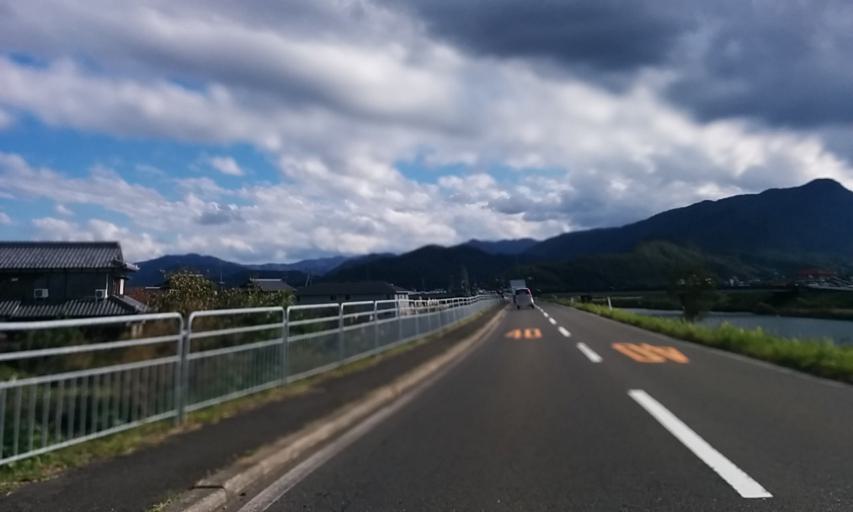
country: JP
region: Fukui
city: Obama
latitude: 35.4982
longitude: 135.7529
